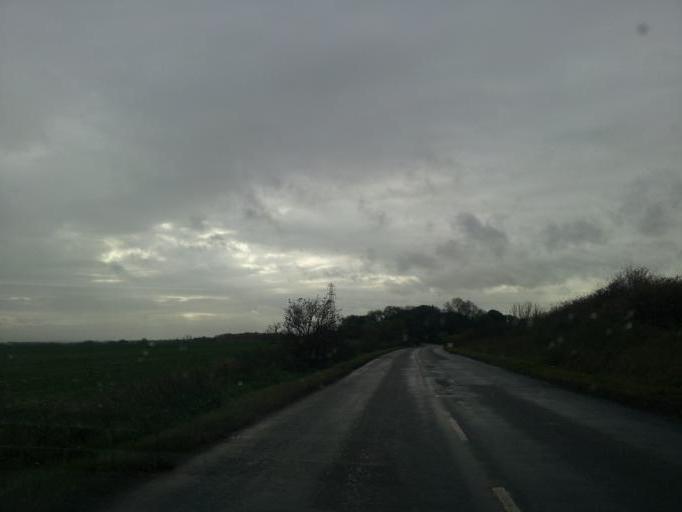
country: GB
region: England
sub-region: Nottinghamshire
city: Newark on Trent
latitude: 53.0227
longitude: -0.8026
